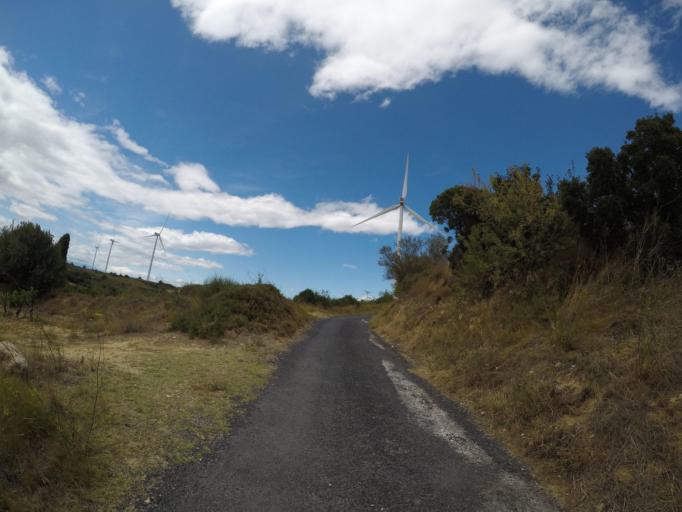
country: FR
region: Languedoc-Roussillon
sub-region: Departement des Pyrenees-Orientales
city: Pezilla-la-Riviere
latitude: 42.7171
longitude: 2.7625
